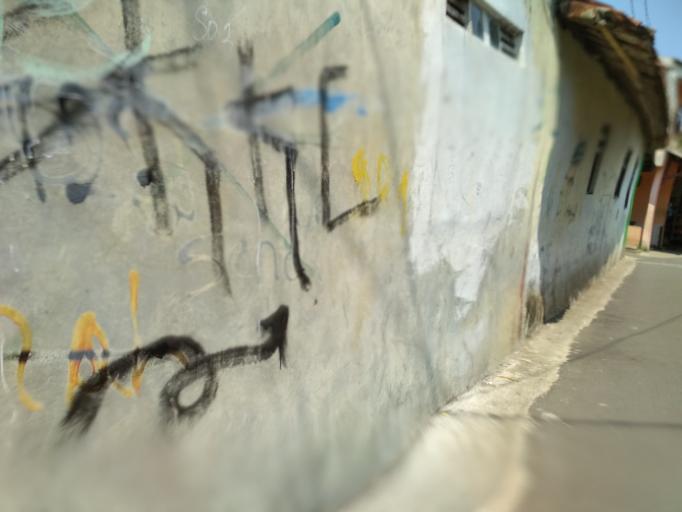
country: ID
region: West Java
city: Ciampea
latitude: -6.5641
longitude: 106.7495
